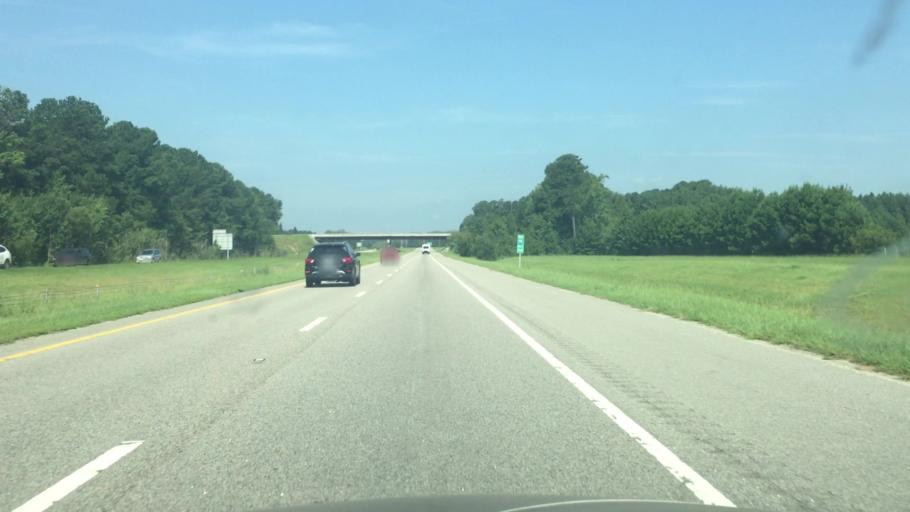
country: US
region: North Carolina
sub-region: Robeson County
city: Lumberton
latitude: 34.5885
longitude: -79.0646
